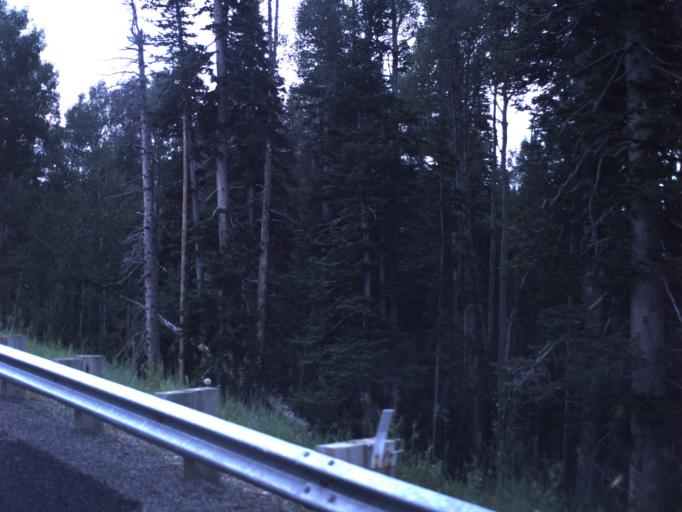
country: US
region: Utah
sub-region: Summit County
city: Francis
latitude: 40.4939
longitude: -111.0350
